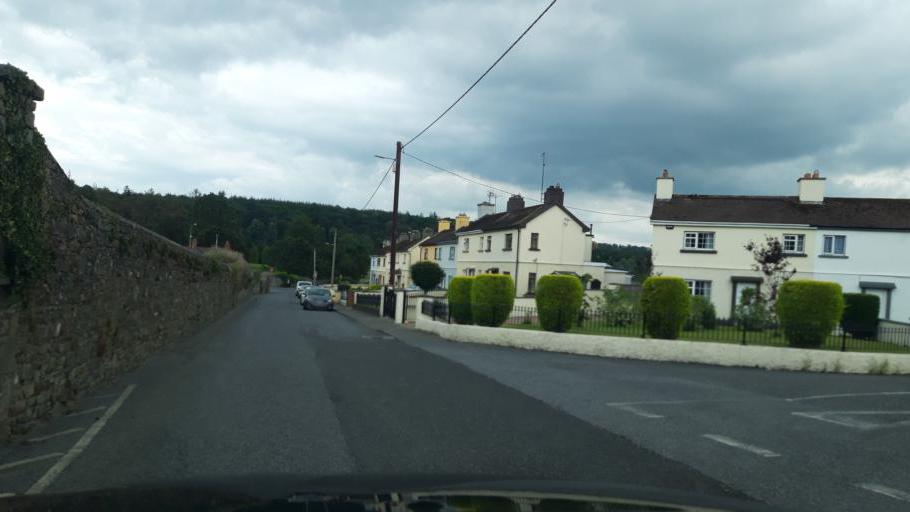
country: IE
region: Leinster
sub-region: Kilkenny
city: Castlecomer
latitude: 52.8016
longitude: -7.2119
